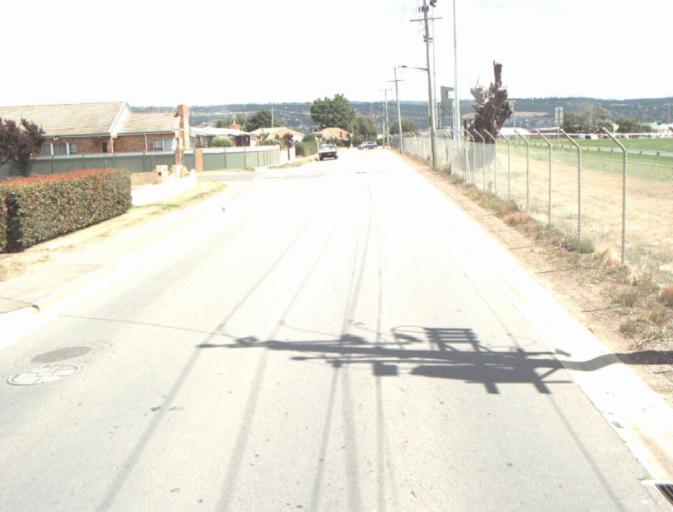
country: AU
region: Tasmania
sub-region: Launceston
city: Newnham
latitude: -41.4062
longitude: 147.1446
